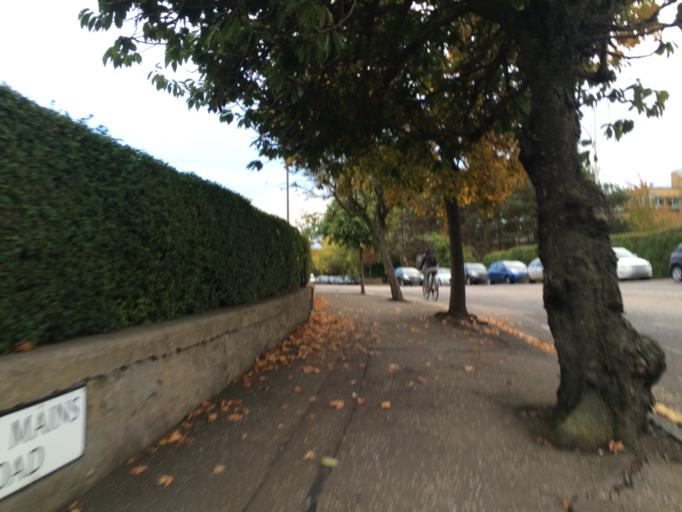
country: GB
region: Scotland
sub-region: Edinburgh
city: Edinburgh
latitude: 55.9248
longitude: -3.1806
